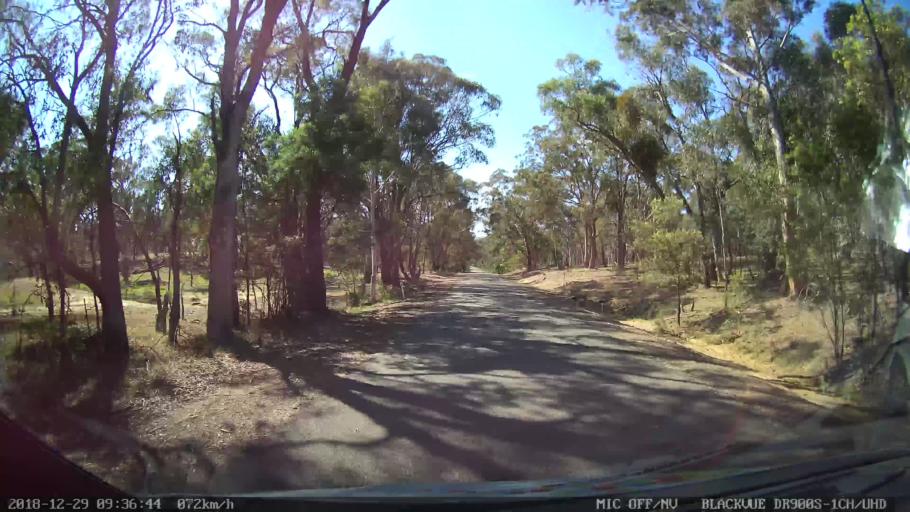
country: AU
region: New South Wales
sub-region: Upper Lachlan Shire
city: Crookwell
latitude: -34.6350
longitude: 149.3672
